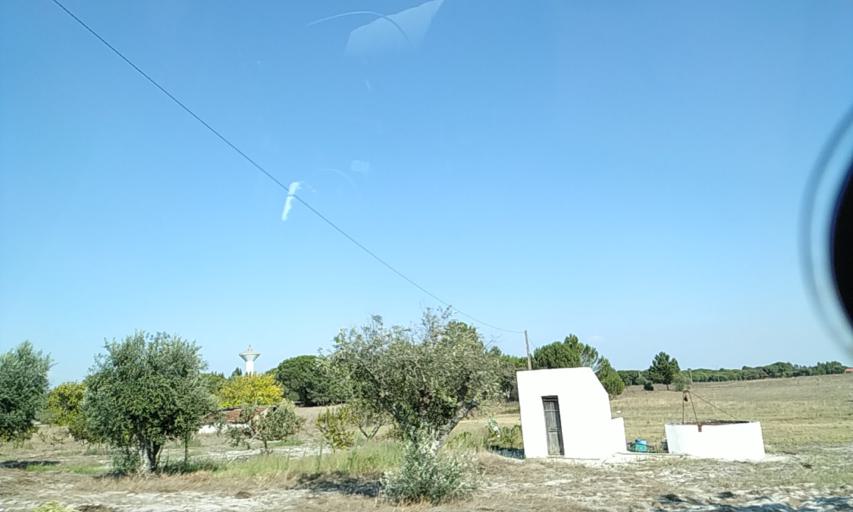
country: PT
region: Santarem
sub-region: Coruche
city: Coruche
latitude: 38.8268
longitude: -8.5643
